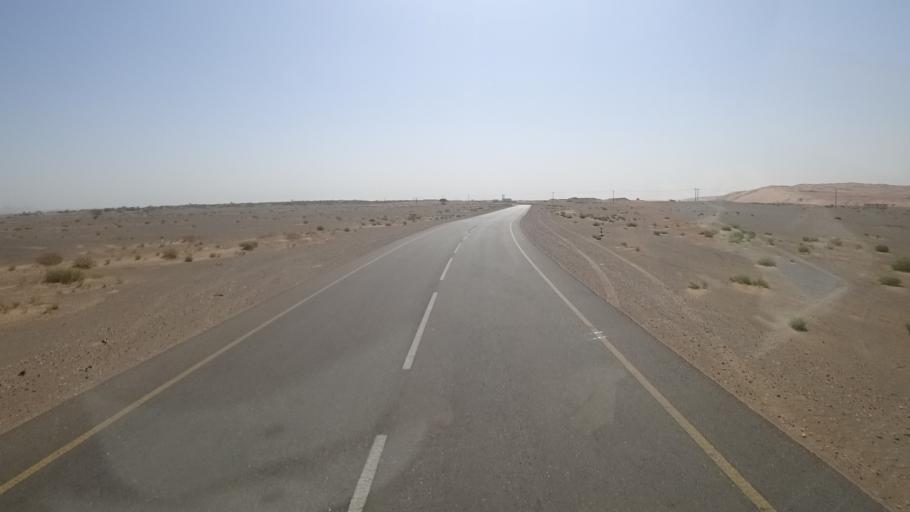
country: OM
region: Ash Sharqiyah
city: Al Qabil
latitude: 22.5000
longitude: 58.7241
